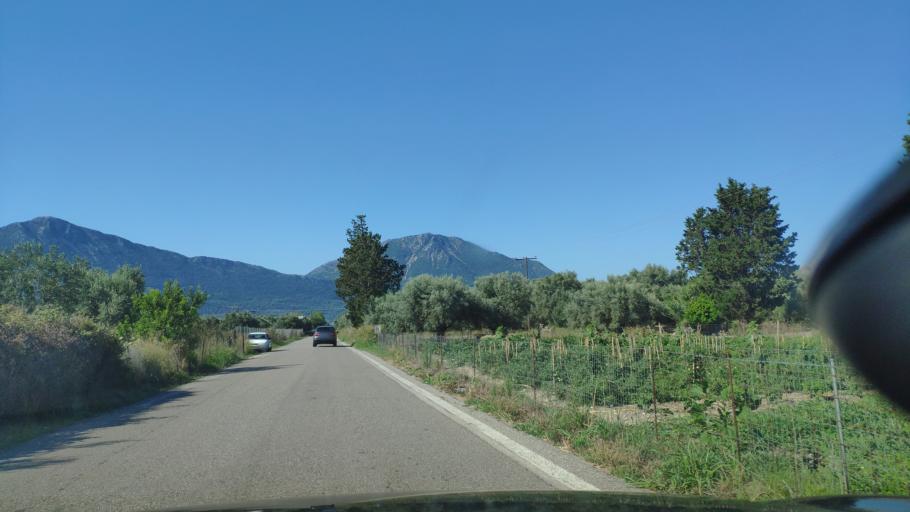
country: GR
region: West Greece
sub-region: Nomos Aitolias kai Akarnanias
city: Kandila
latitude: 38.6854
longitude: 20.9436
